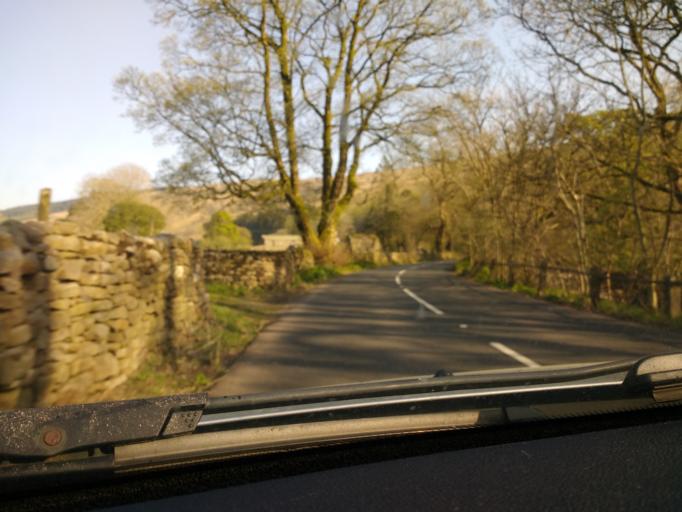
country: GB
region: England
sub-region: Cumbria
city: Sedbergh
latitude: 54.3028
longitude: -2.4070
